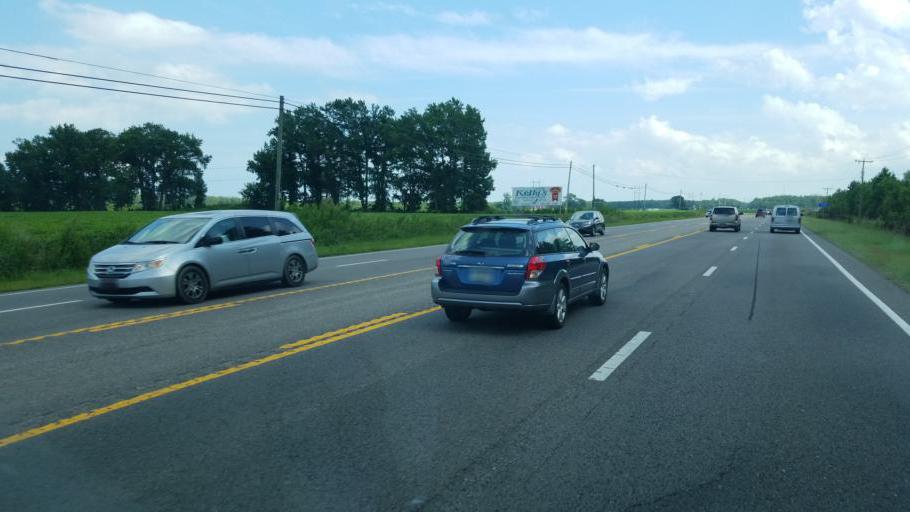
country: US
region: North Carolina
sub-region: Currituck County
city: Currituck
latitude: 36.3177
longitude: -75.9377
